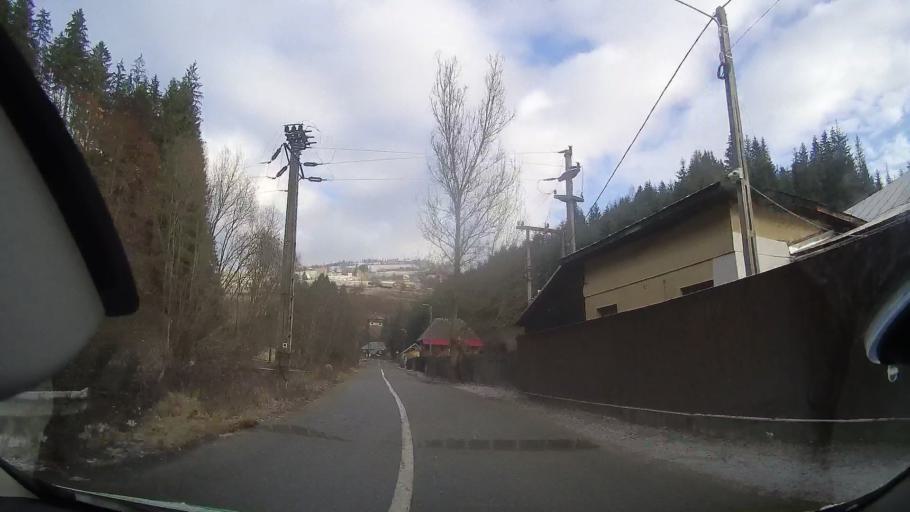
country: RO
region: Alba
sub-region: Comuna Albac
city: Albac
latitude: 46.4674
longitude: 22.9678
